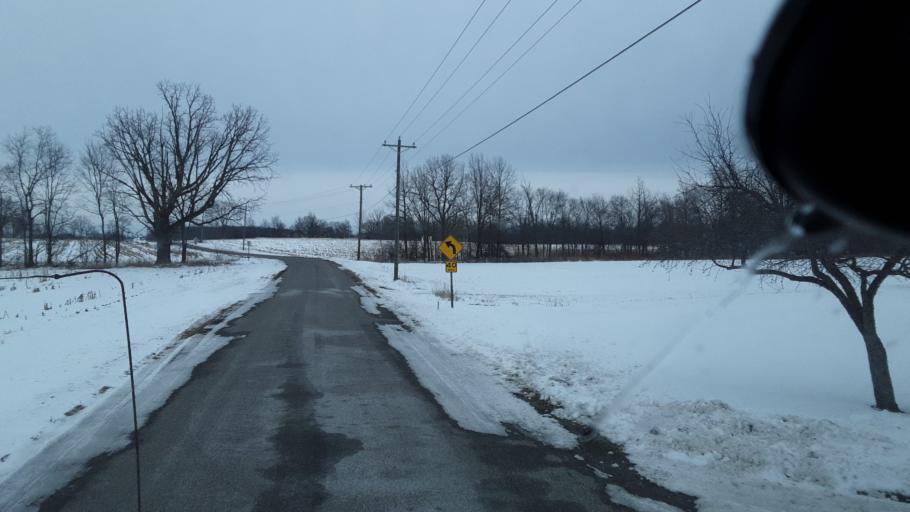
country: US
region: Ohio
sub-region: Madison County
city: Plain City
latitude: 40.1603
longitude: -83.3277
